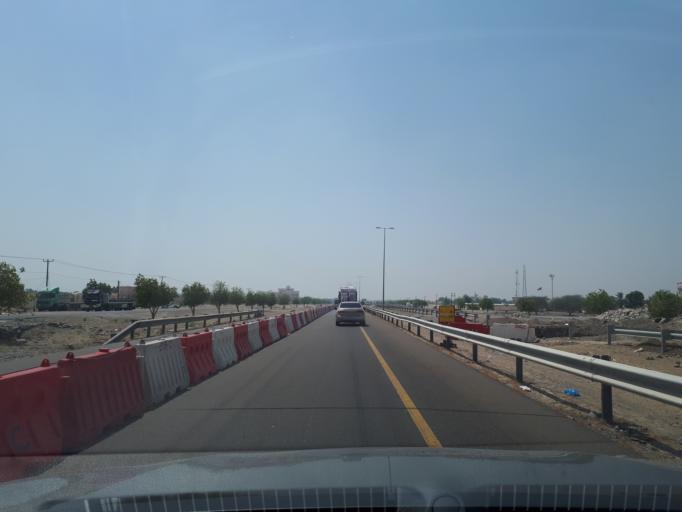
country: OM
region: Al Batinah
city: Al Liwa'
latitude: 24.5749
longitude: 56.5446
